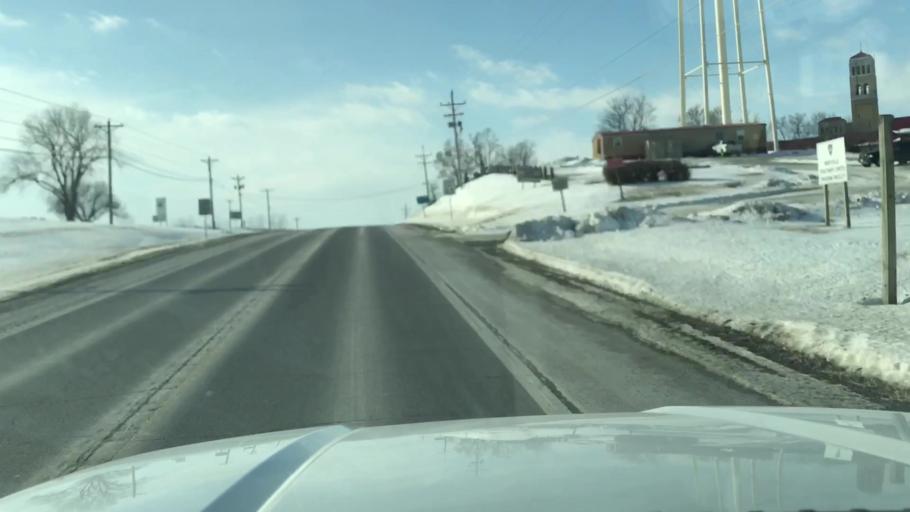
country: US
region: Missouri
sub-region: Nodaway County
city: Maryville
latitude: 40.3448
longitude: -94.8109
